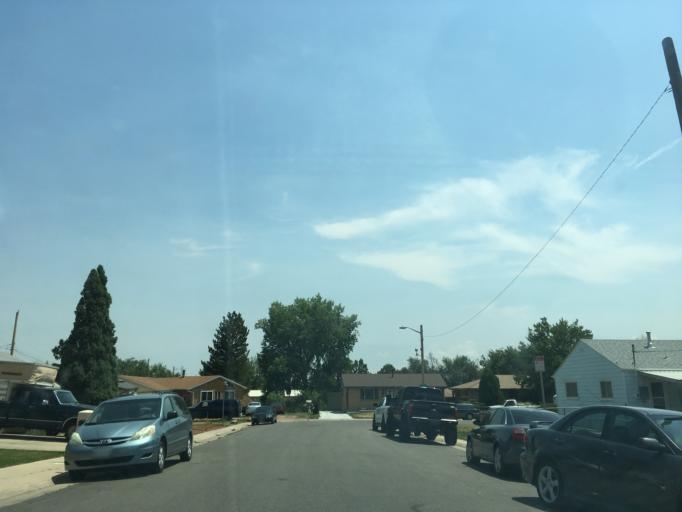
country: US
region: Colorado
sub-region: Jefferson County
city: Lakewood
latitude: 39.6977
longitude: -105.0326
